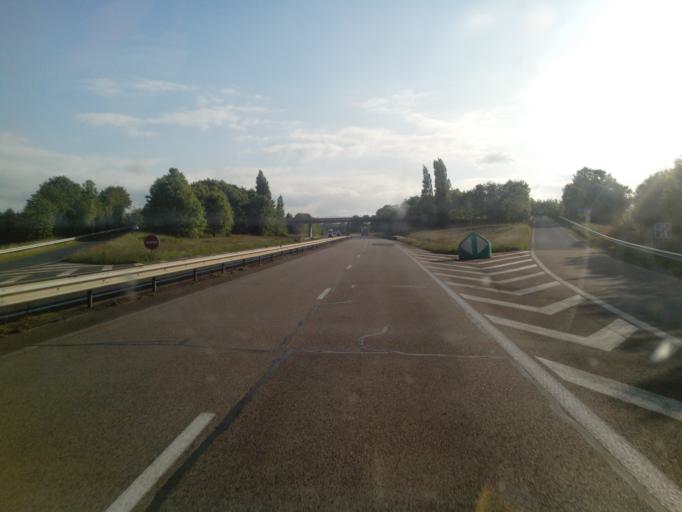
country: FR
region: Lower Normandy
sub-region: Departement du Calvados
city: Grainville-sur-Odon
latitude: 49.1126
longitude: -0.5922
